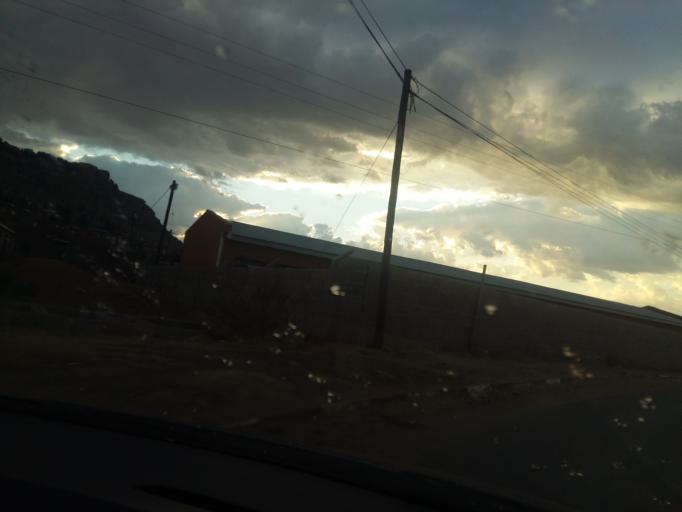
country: LS
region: Maseru
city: Maseru
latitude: -29.3607
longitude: 27.4646
